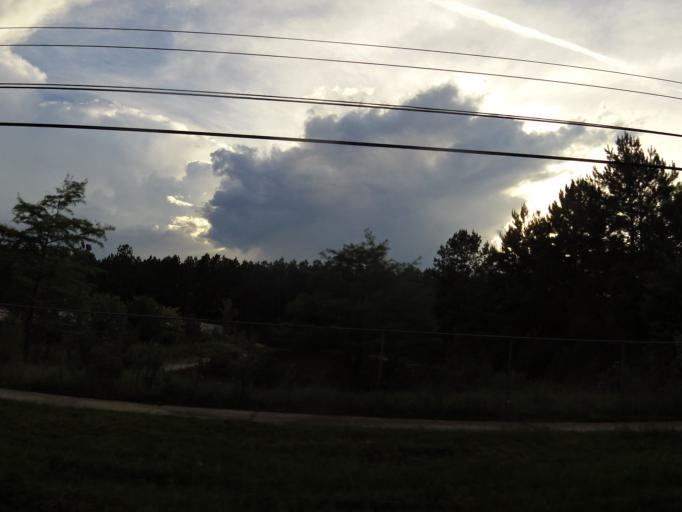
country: US
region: Florida
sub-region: Duval County
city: Jacksonville
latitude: 30.3603
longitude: -81.7731
